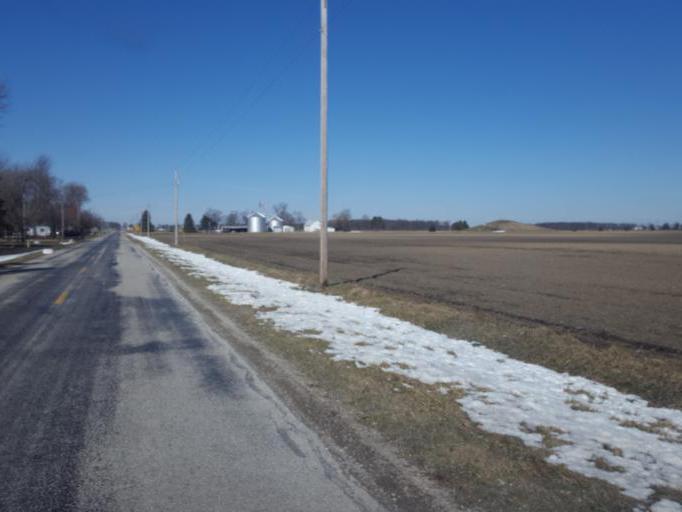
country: US
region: Ohio
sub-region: Marion County
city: Marion
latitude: 40.6521
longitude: -83.0855
